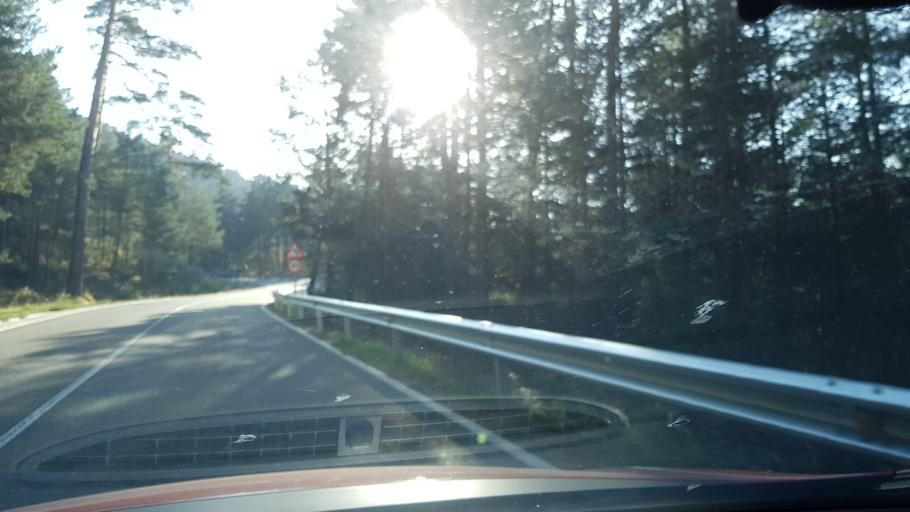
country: ES
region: Madrid
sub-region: Provincia de Madrid
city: Cercedilla
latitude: 40.8144
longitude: -4.0181
